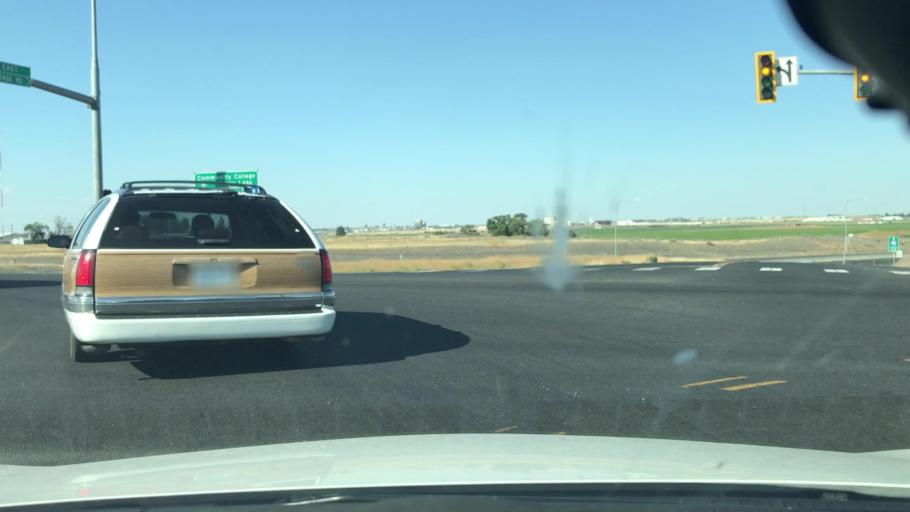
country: US
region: Washington
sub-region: Grant County
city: Moses Lake
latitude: 47.0978
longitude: -119.2427
